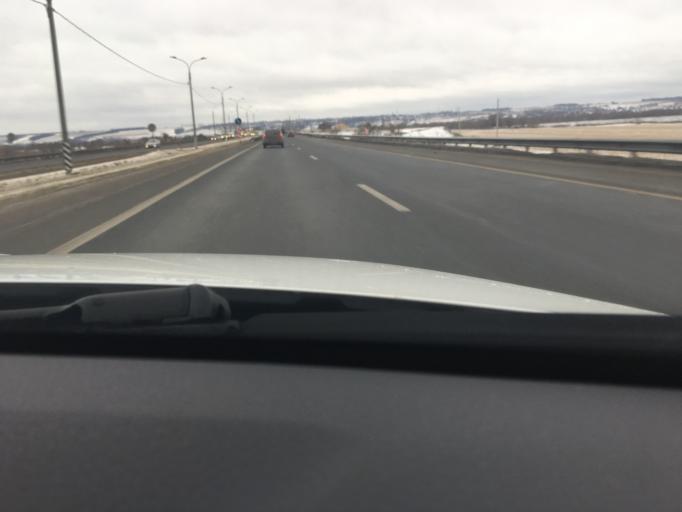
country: RU
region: Moskovskaya
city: Danki
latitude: 54.8783
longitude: 37.5083
